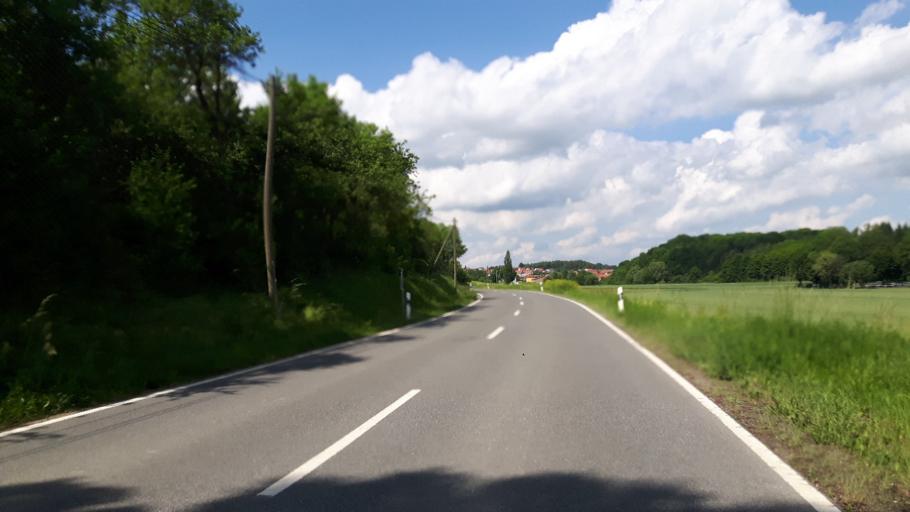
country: DE
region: Bavaria
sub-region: Regierungsbezirk Unterfranken
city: Kirchheim
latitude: 49.6448
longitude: 9.8525
